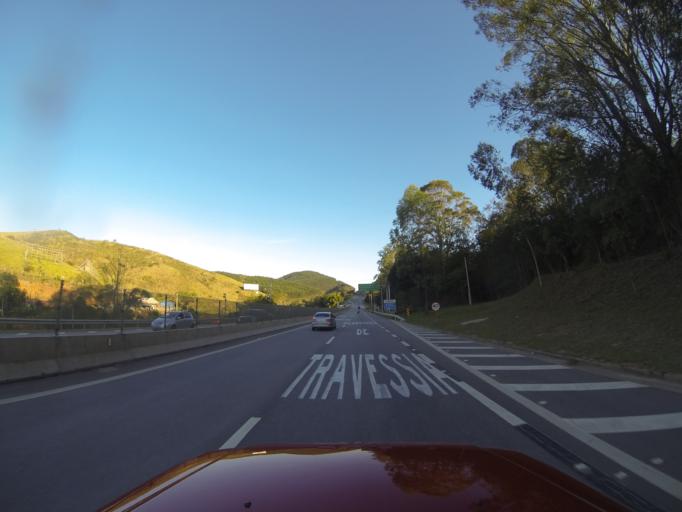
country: BR
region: Sao Paulo
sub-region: Santa Branca
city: Santa Branca
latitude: -23.3230
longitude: -45.7184
